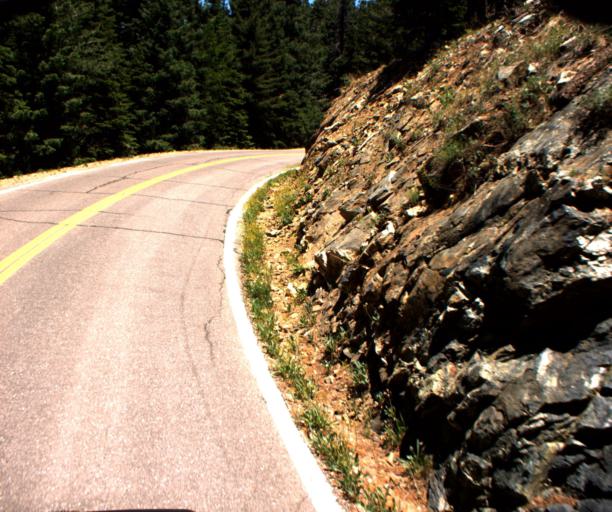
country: US
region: Arizona
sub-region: Graham County
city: Swift Trail Junction
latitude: 32.6529
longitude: -109.8604
